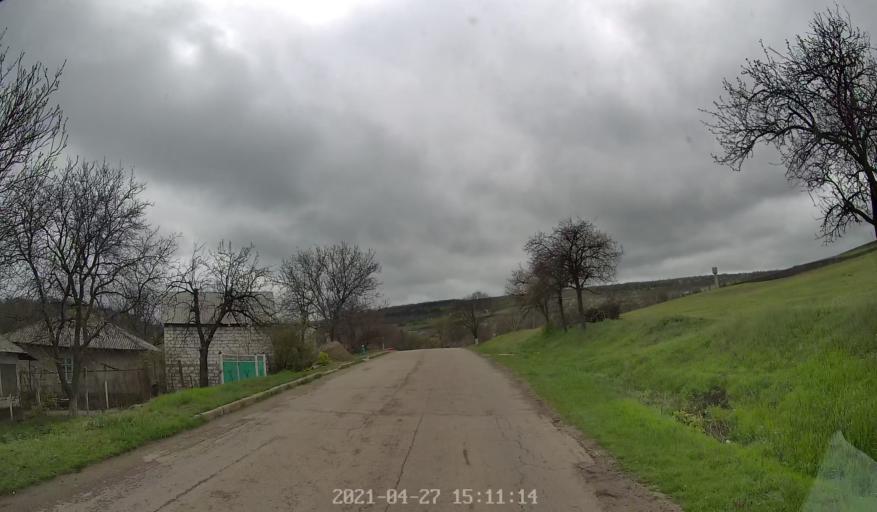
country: MD
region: Chisinau
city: Vadul lui Voda
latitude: 47.0332
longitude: 29.0288
